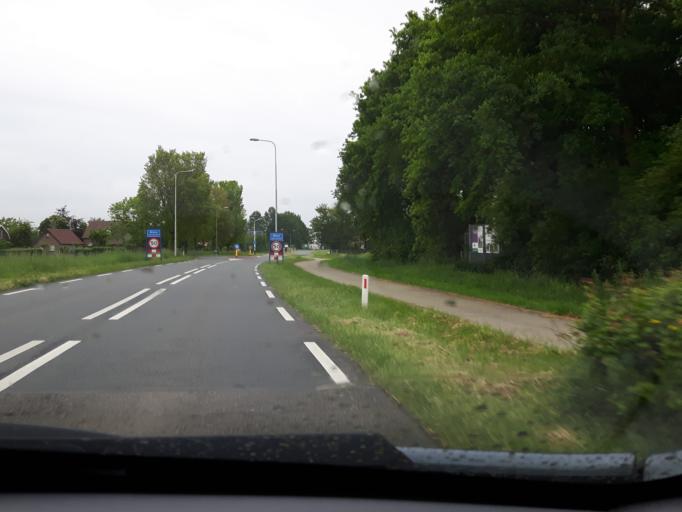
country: NL
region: Zeeland
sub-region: Gemeente Goes
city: Goes
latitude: 51.4585
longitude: 3.8515
